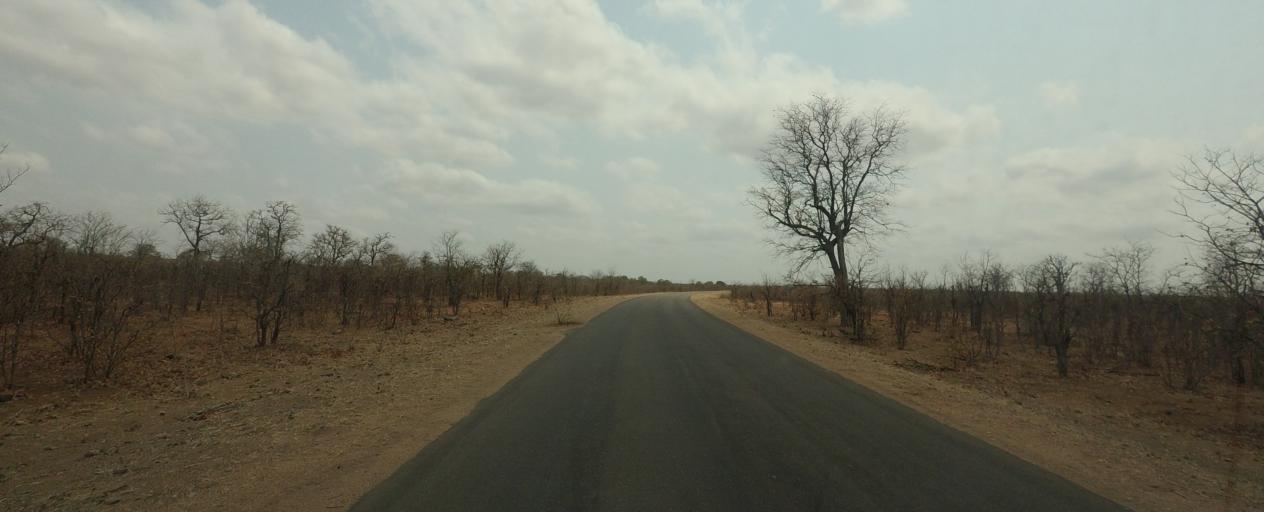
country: ZA
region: Limpopo
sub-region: Mopani District Municipality
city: Phalaborwa
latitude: -23.5491
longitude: 31.4294
